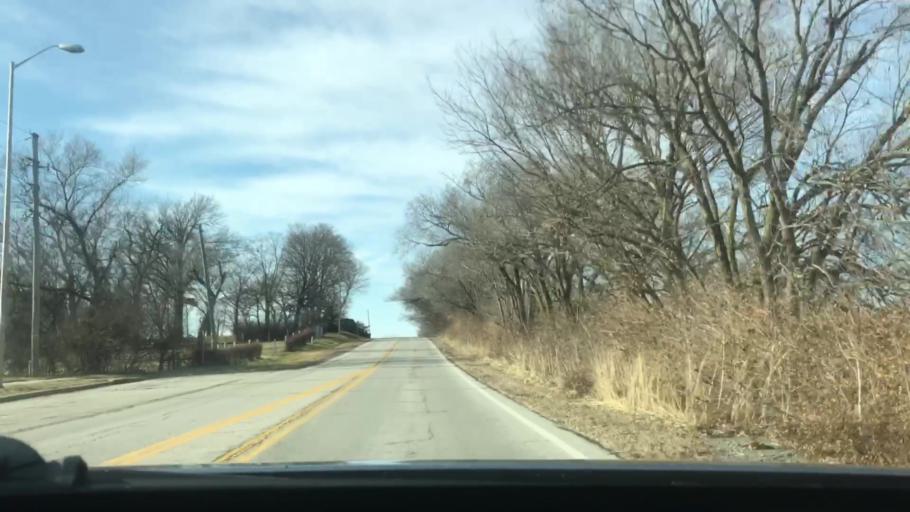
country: US
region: Missouri
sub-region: Clay County
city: Smithville
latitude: 39.3039
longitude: -94.5928
